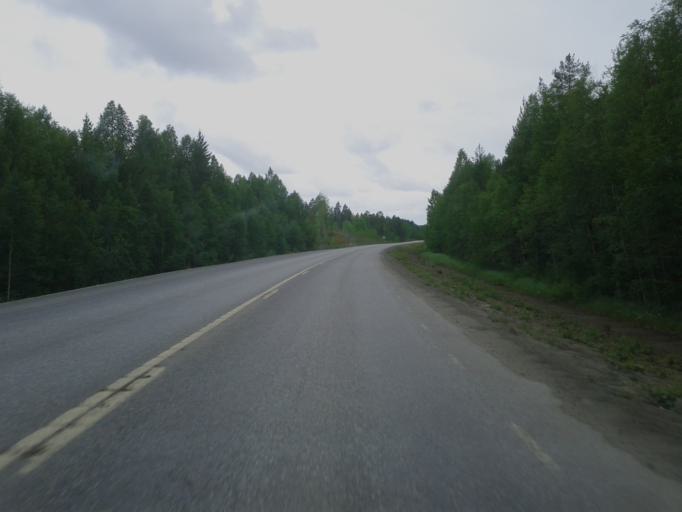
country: SE
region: Vaesterbotten
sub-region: Skelleftea Kommun
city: Boliden
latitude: 64.8744
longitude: 20.3528
